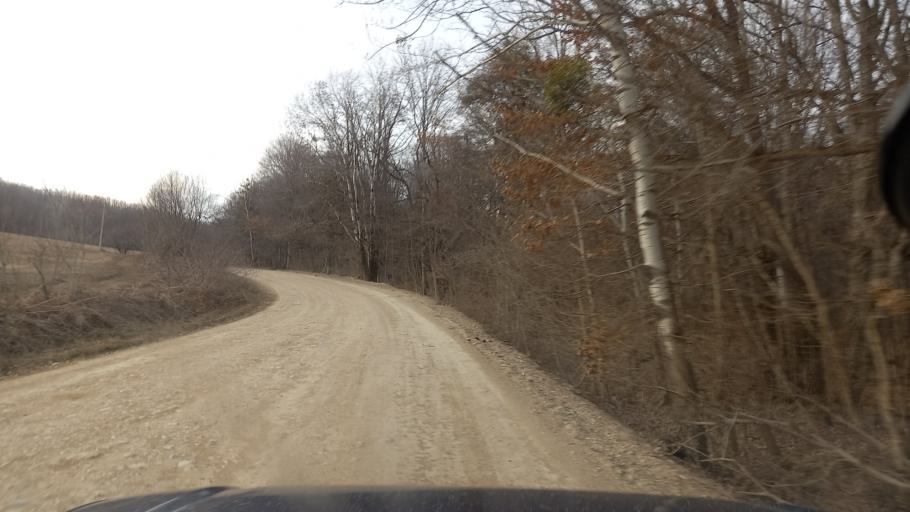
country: RU
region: Adygeya
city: Kamennomostskiy
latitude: 44.1462
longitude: 40.2512
